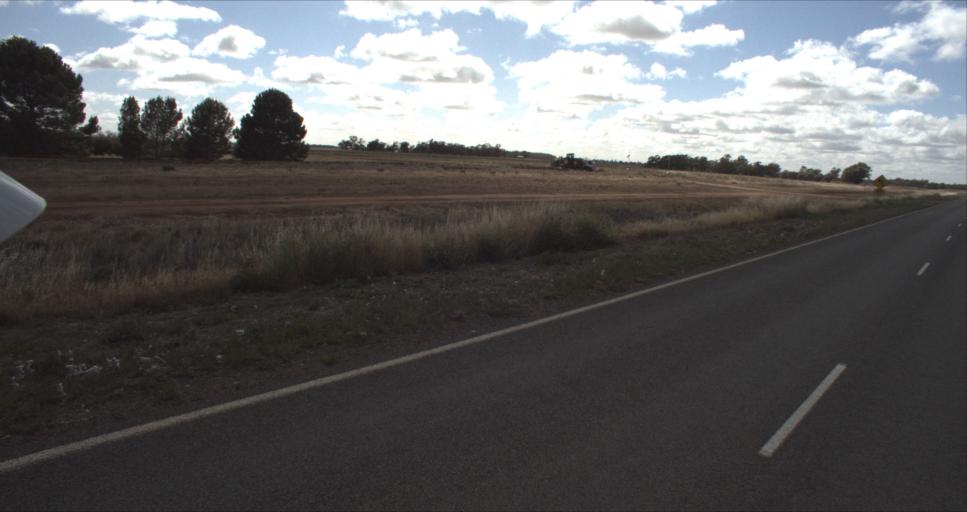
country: AU
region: New South Wales
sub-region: Murrumbidgee Shire
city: Darlington Point
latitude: -34.5924
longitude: 146.1397
